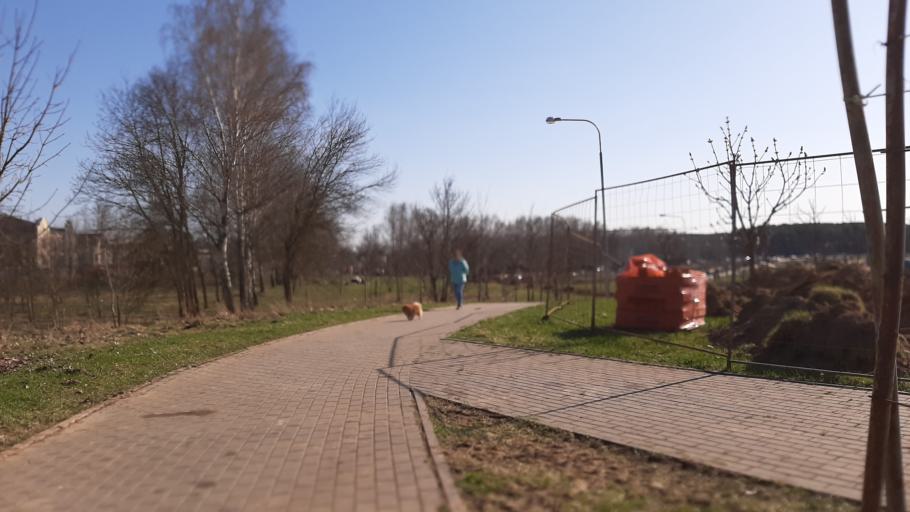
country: BY
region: Minsk
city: Bal'shavik
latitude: 53.9565
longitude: 27.5873
